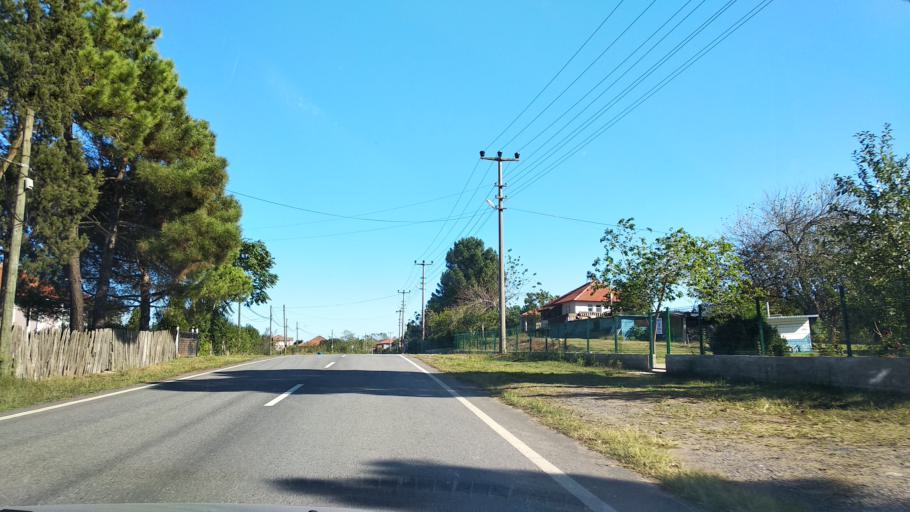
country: TR
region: Sakarya
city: Karasu
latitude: 41.1183
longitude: 30.6182
